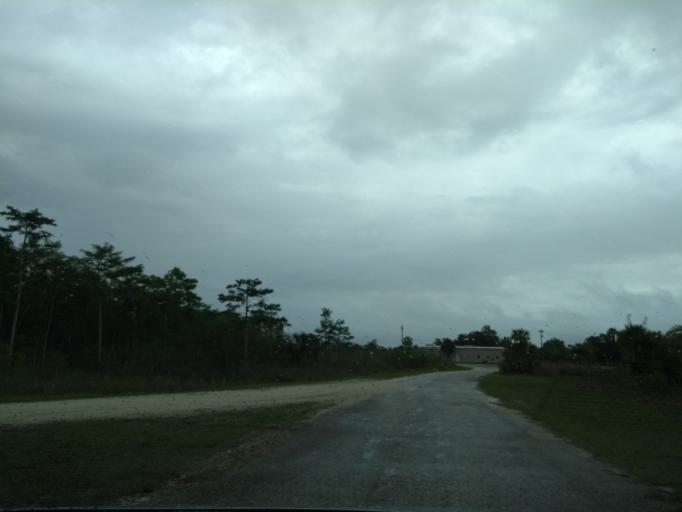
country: US
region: Florida
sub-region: Collier County
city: Lely Resort
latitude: 25.9527
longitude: -81.3627
